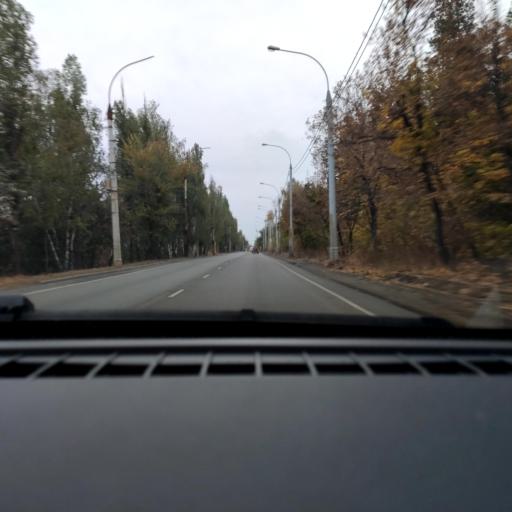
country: RU
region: Voronezj
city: Somovo
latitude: 51.7066
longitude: 39.2913
